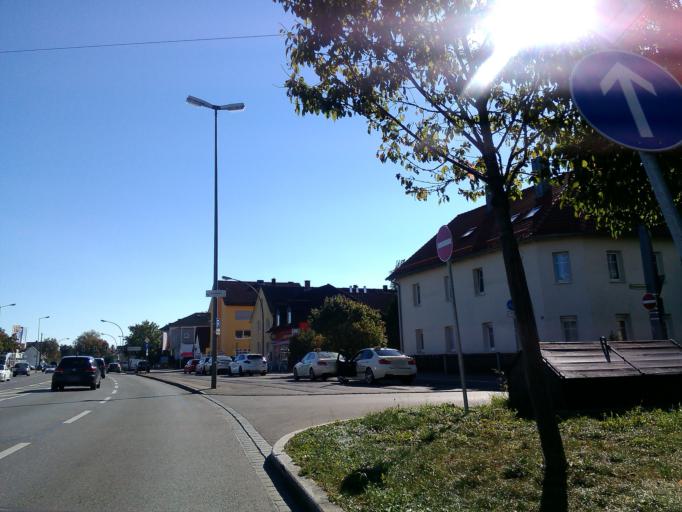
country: DE
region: Bavaria
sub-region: Swabia
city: Konigsbrunn
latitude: 48.3189
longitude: 10.9090
